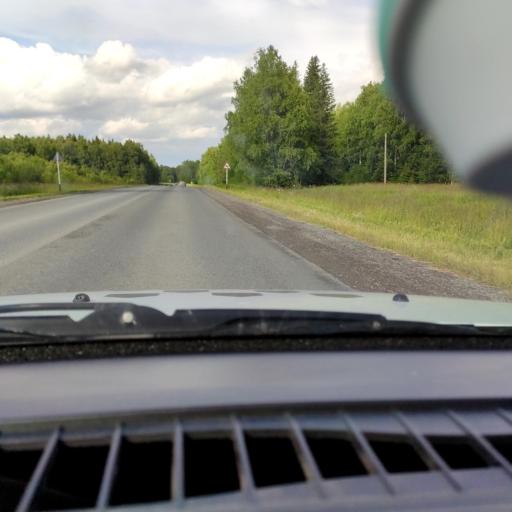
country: RU
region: Perm
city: Orda
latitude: 57.2455
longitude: 56.9922
